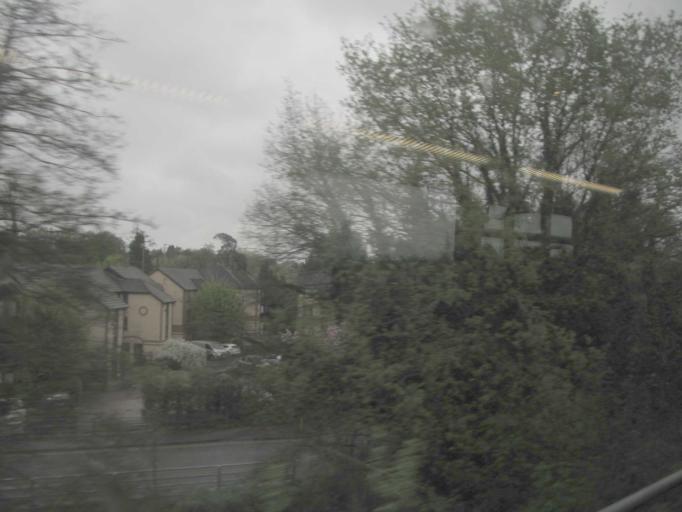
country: GB
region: England
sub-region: Wokingham
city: Wokingham
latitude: 51.4043
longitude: -0.8392
